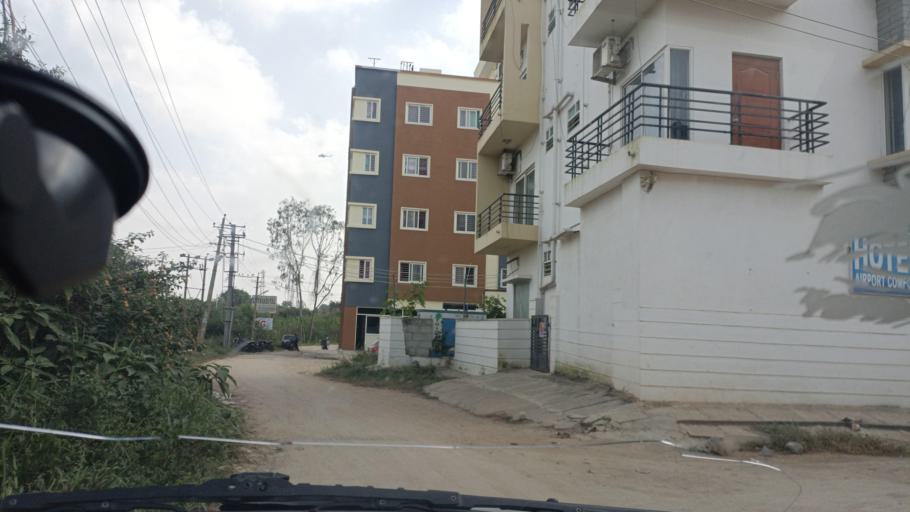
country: IN
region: Karnataka
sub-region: Bangalore Urban
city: Yelahanka
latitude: 13.1481
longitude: 77.6202
